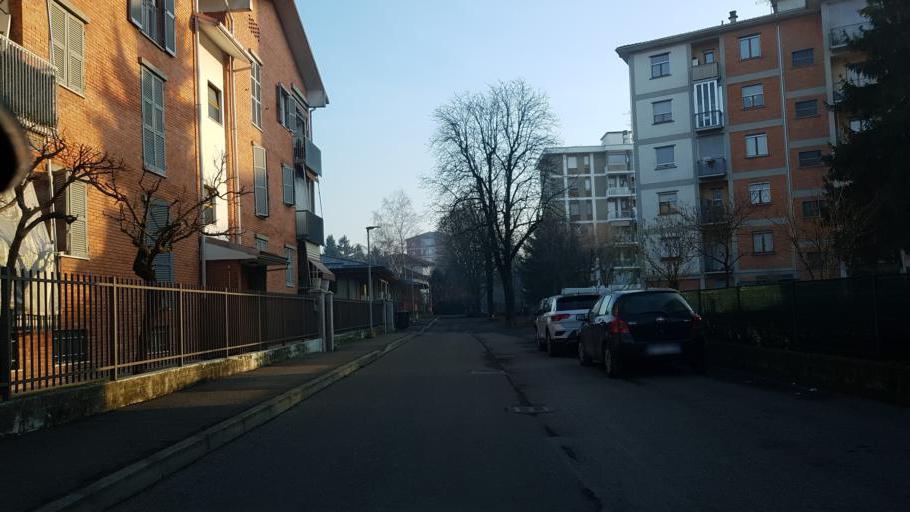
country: IT
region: Piedmont
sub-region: Provincia di Alessandria
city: Novi Ligure
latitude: 44.7679
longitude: 8.8002
